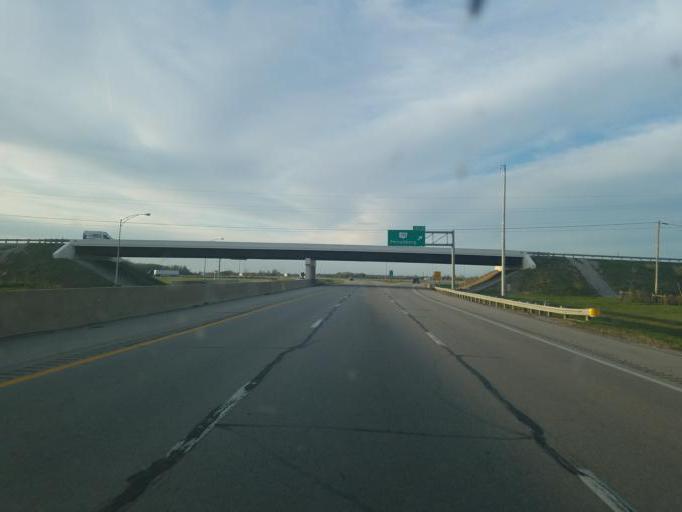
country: US
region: Ohio
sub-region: Wood County
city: Millbury
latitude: 41.5579
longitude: -83.4604
